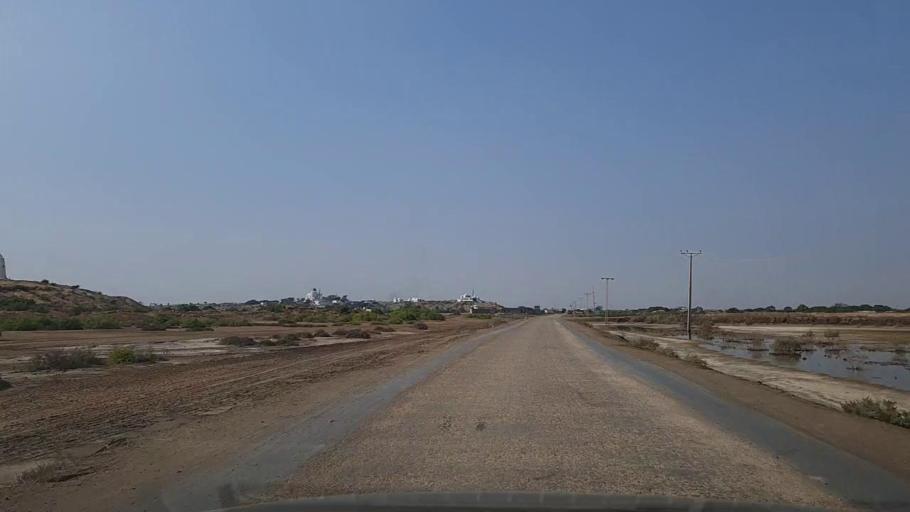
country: PK
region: Sindh
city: Chuhar Jamali
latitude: 24.5548
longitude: 67.8888
